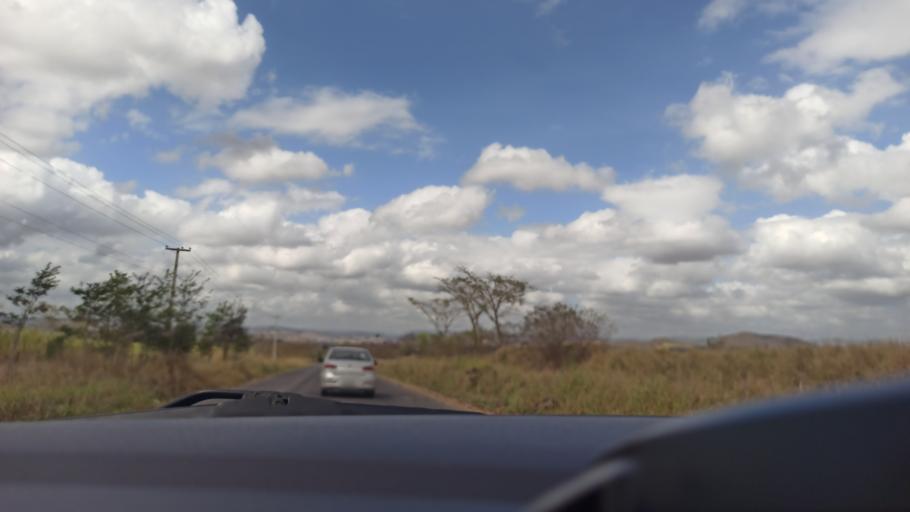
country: BR
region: Pernambuco
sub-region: Timbauba
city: Timbauba
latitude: -7.4728
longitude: -35.2771
